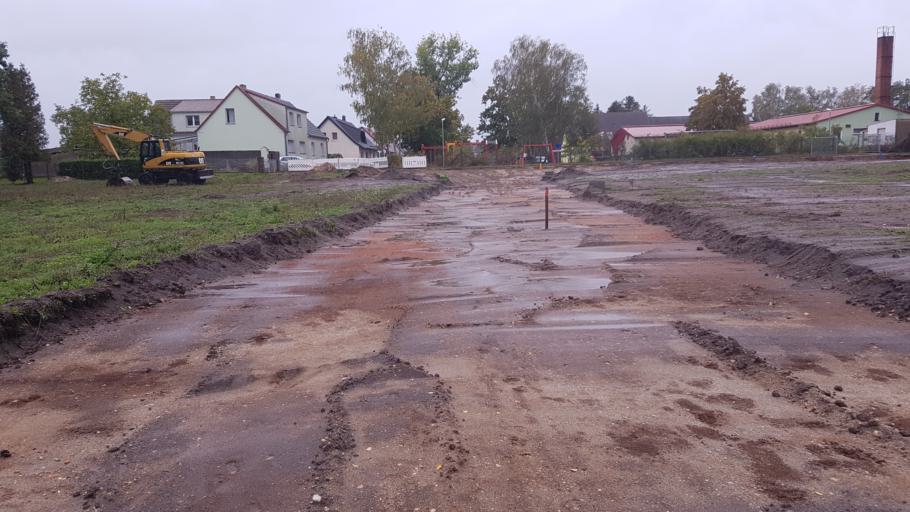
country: DE
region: Brandenburg
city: Schonborn
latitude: 51.6006
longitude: 13.4967
